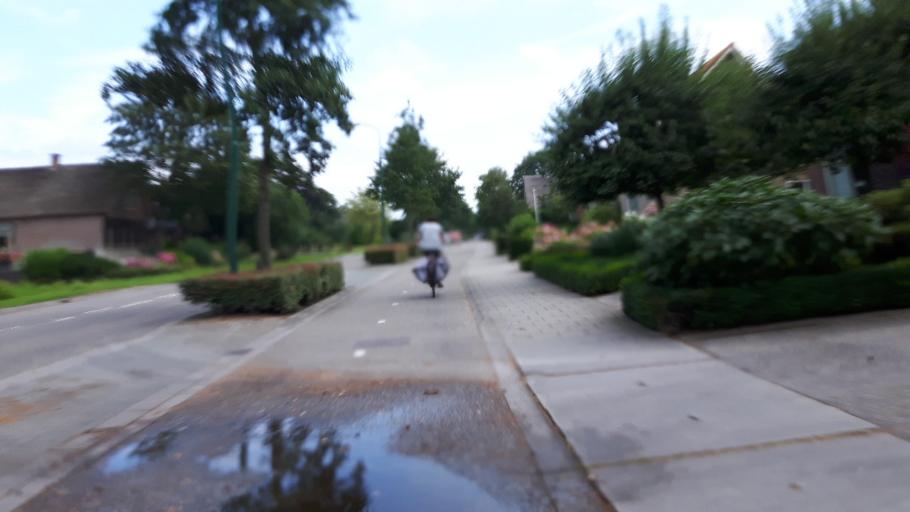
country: NL
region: Utrecht
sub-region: Gemeente Woerden
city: Woerden
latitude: 52.1143
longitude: 4.8386
